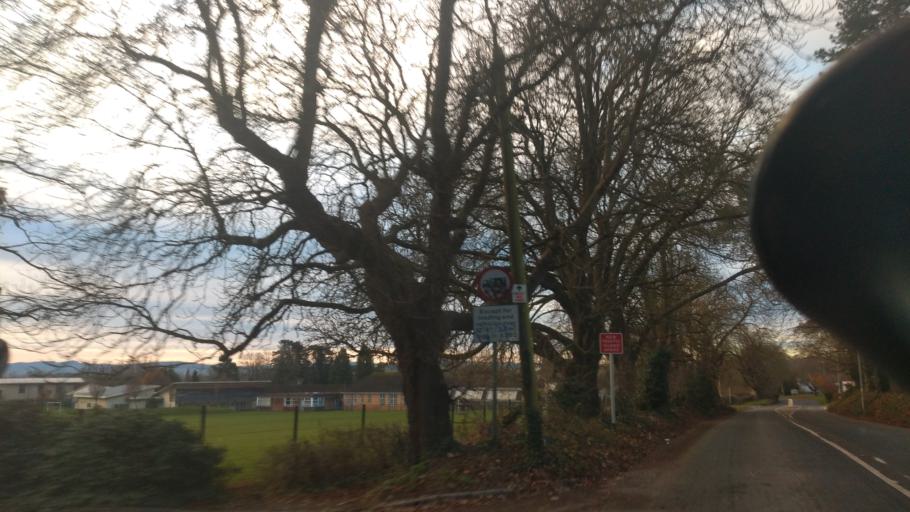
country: GB
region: England
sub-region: Somerset
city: Frome
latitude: 51.2450
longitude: -2.3110
